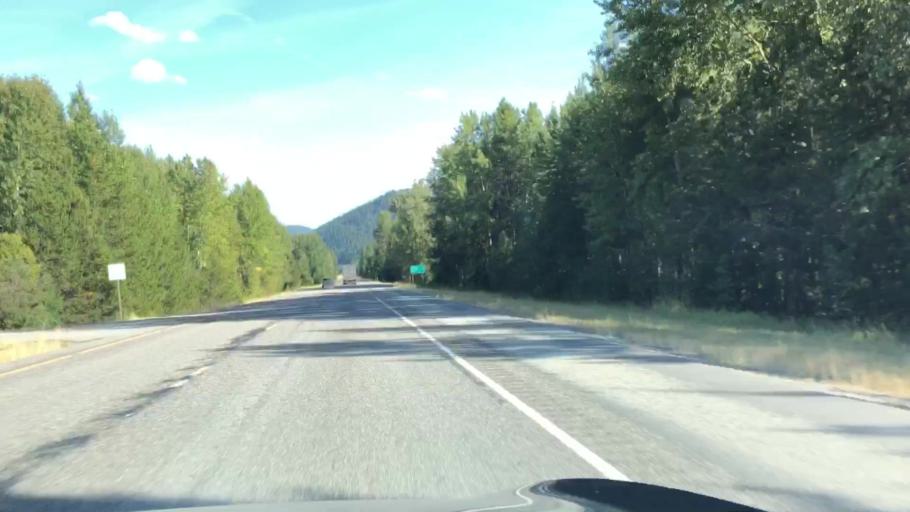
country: US
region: Montana
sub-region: Sanders County
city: Thompson Falls
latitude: 47.3696
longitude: -115.3374
